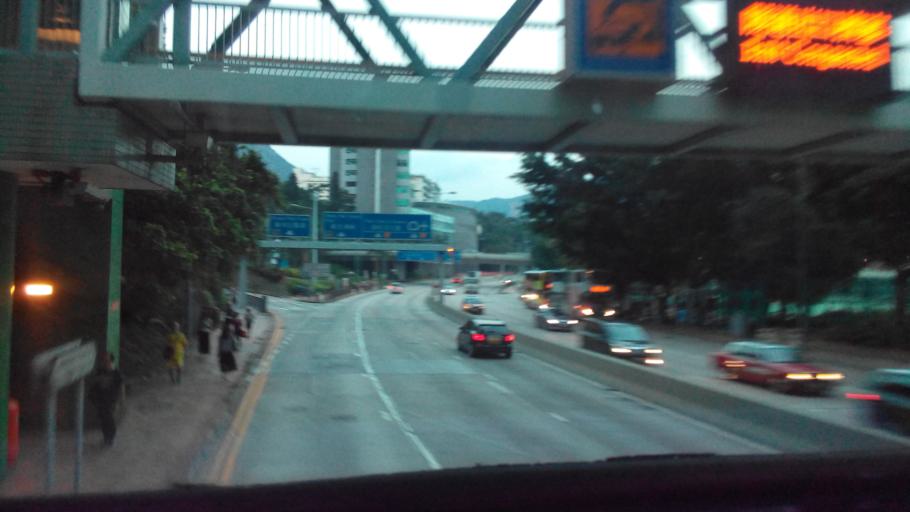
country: HK
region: Wanchai
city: Wan Chai
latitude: 22.2502
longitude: 114.1693
